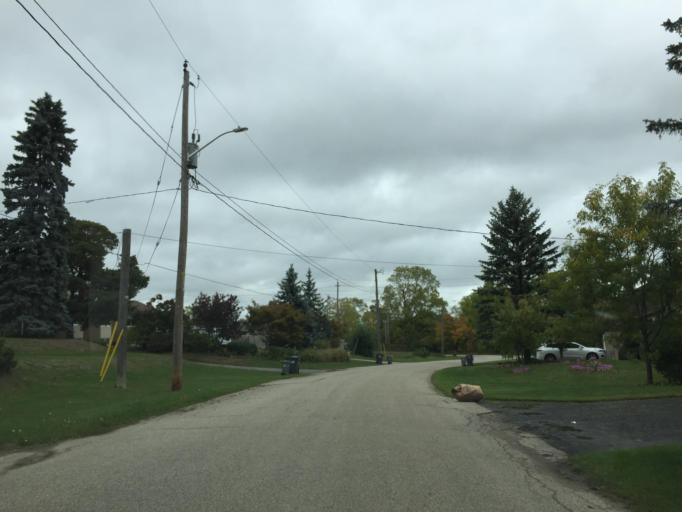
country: CA
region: Ontario
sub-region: Wellington County
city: Guelph
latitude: 43.5171
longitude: -80.2503
